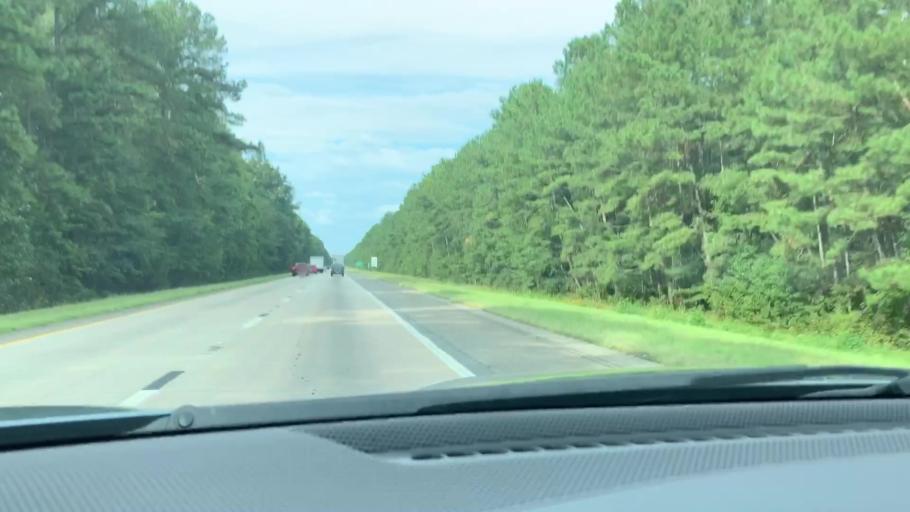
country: US
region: South Carolina
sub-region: Colleton County
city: Walterboro
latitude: 32.9796
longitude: -80.6740
